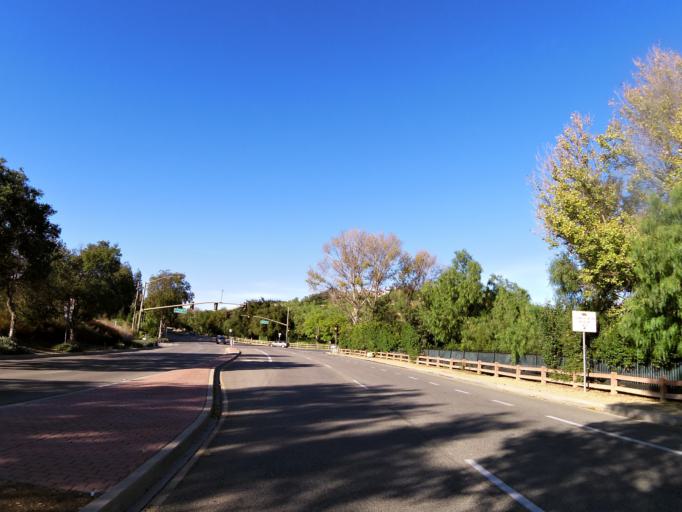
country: US
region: California
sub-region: Ventura County
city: Thousand Oaks
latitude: 34.1959
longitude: -118.8227
